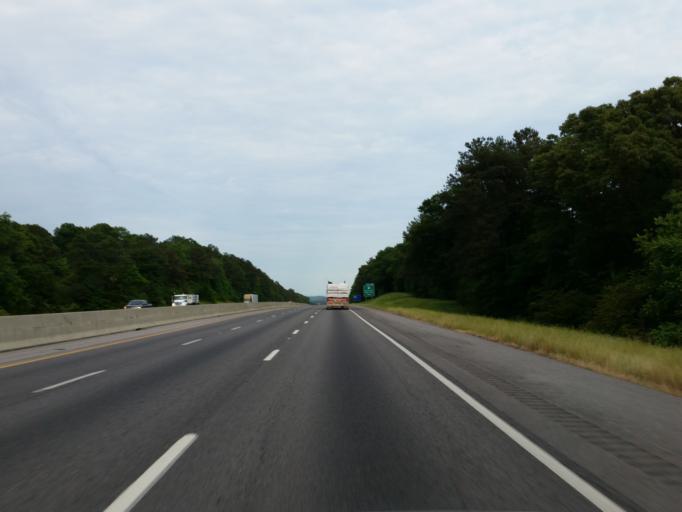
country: US
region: Alabama
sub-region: Saint Clair County
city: Riverside
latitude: 33.6059
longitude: -86.2340
